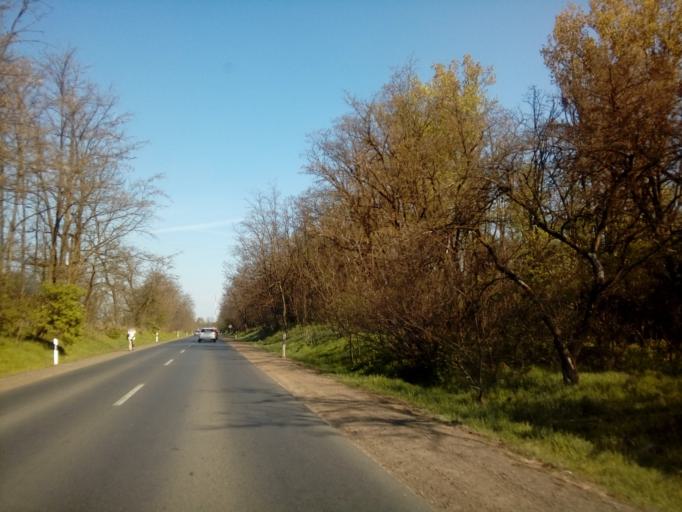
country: HU
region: Szabolcs-Szatmar-Bereg
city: Nyiregyhaza
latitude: 47.9198
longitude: 21.7698
